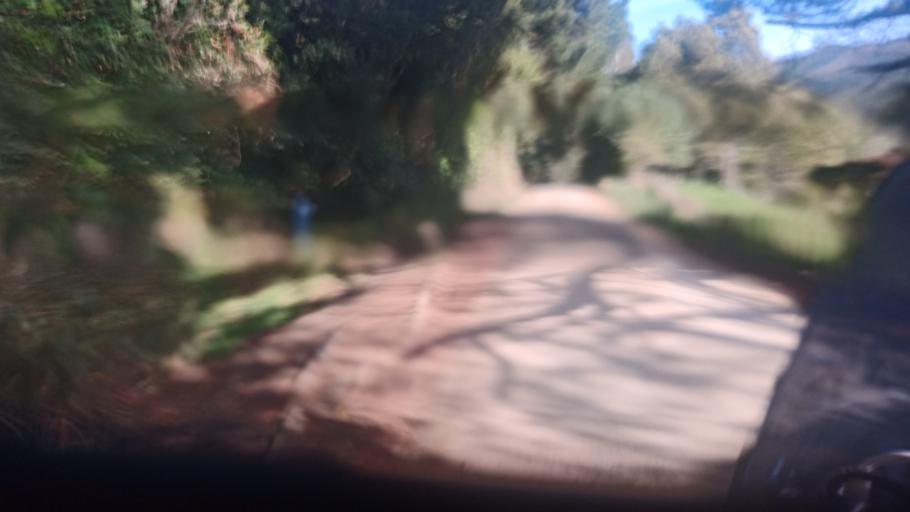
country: NZ
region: Bay of Plenty
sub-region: Opotiki District
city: Opotiki
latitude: -38.4341
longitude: 177.5519
